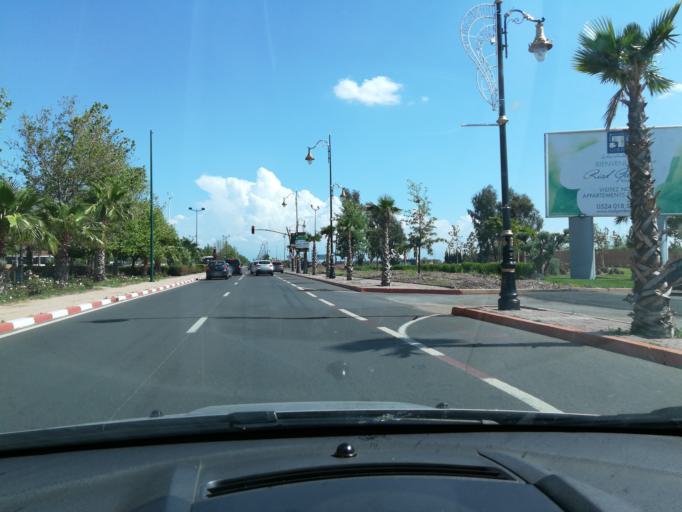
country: MA
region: Marrakech-Tensift-Al Haouz
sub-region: Marrakech
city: Marrakesh
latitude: 31.5960
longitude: -7.9942
